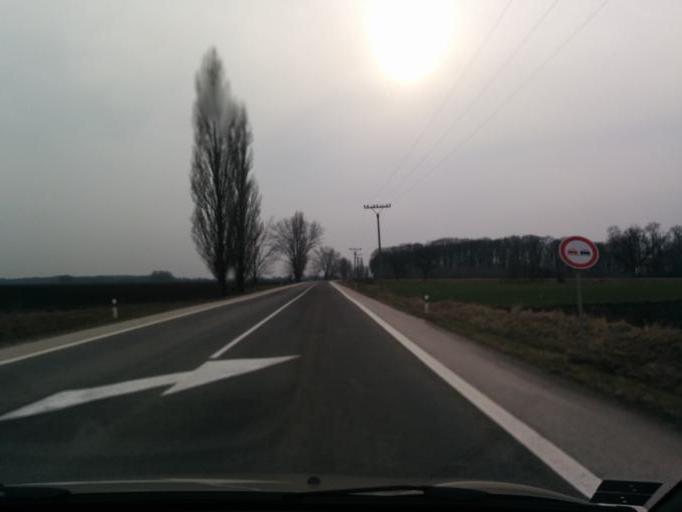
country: SK
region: Trnavsky
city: Sladkovicovo
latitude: 48.2324
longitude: 17.6849
